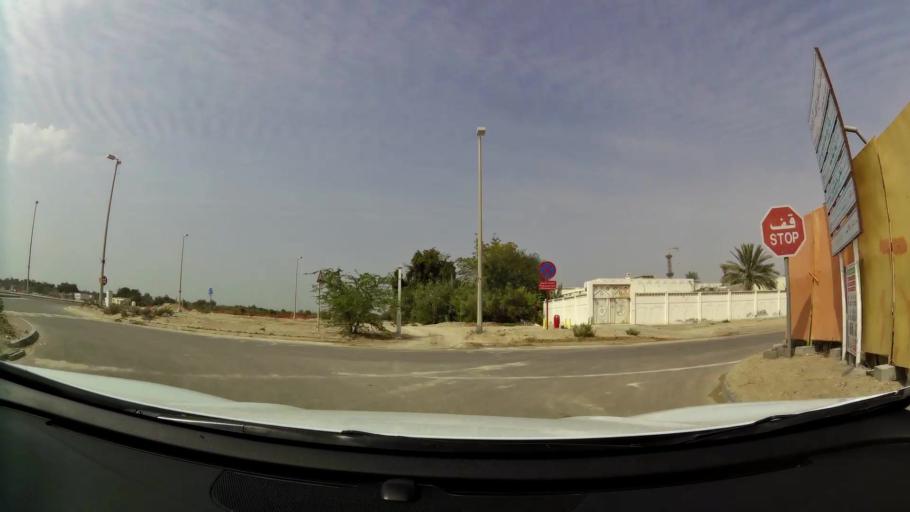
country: AE
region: Abu Dhabi
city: Abu Dhabi
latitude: 24.5515
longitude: 54.6780
